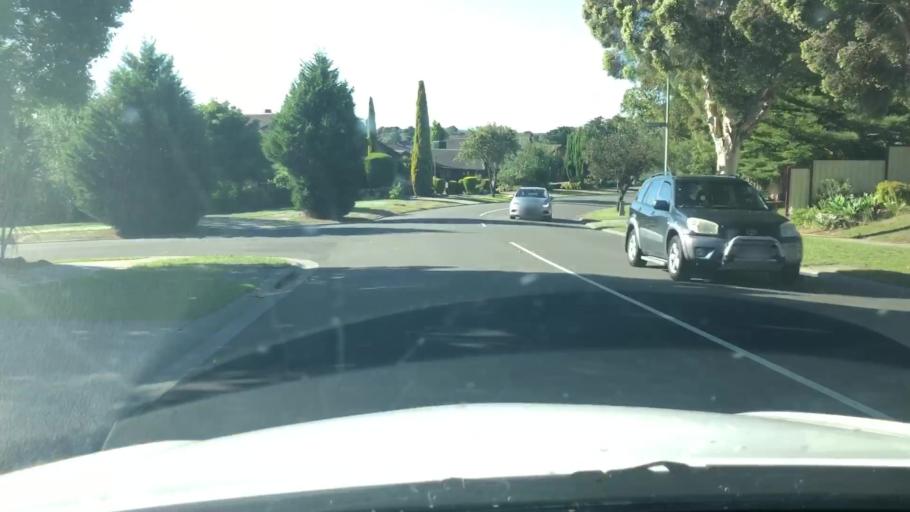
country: AU
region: Victoria
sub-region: Casey
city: Endeavour Hills
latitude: -37.9778
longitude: 145.2496
